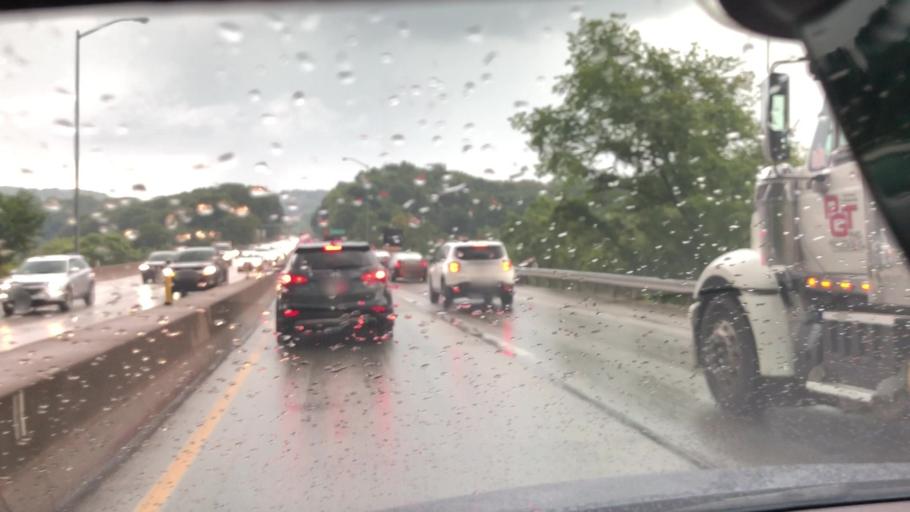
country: US
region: Pennsylvania
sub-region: Allegheny County
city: Homestead
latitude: 40.4253
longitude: -79.9082
